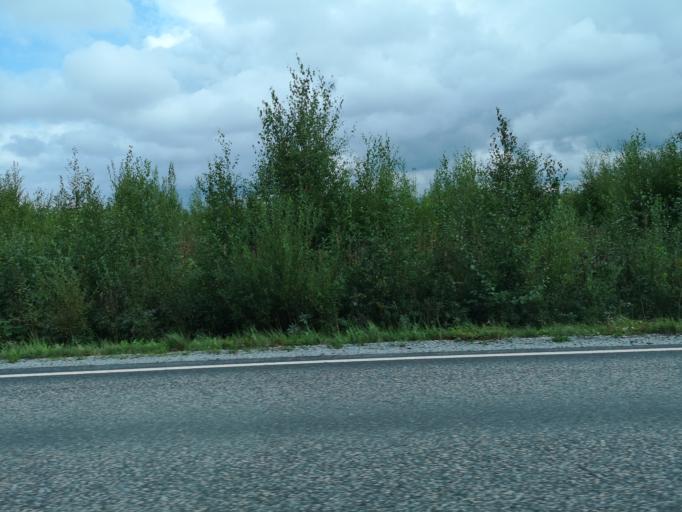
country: FI
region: Central Finland
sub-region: Jyvaeskylae
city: Hankasalmi
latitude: 62.3685
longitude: 26.4459
